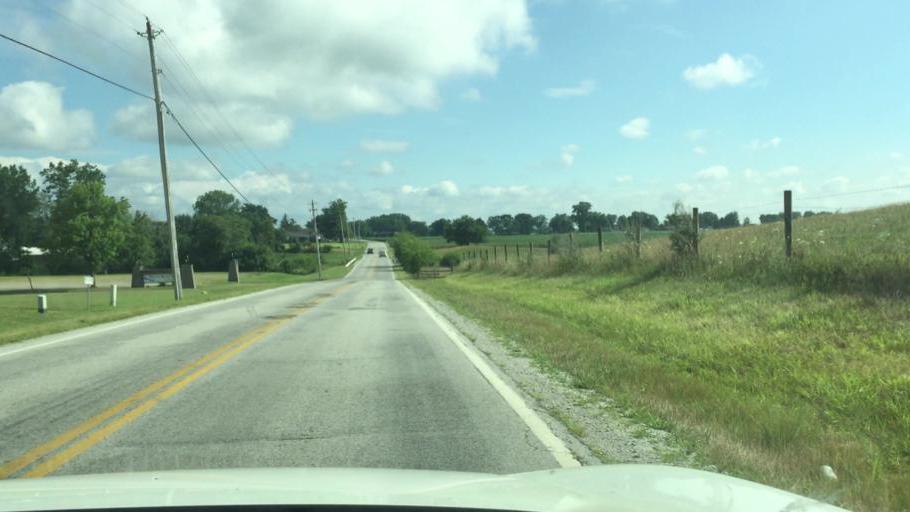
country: US
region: Ohio
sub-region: Clark County
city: Lisbon
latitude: 39.9490
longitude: -83.6814
